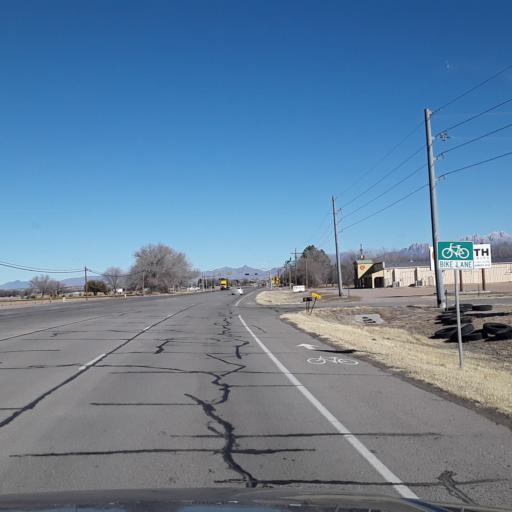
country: US
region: New Mexico
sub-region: Dona Ana County
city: Mesilla
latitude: 32.3013
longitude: -106.8518
